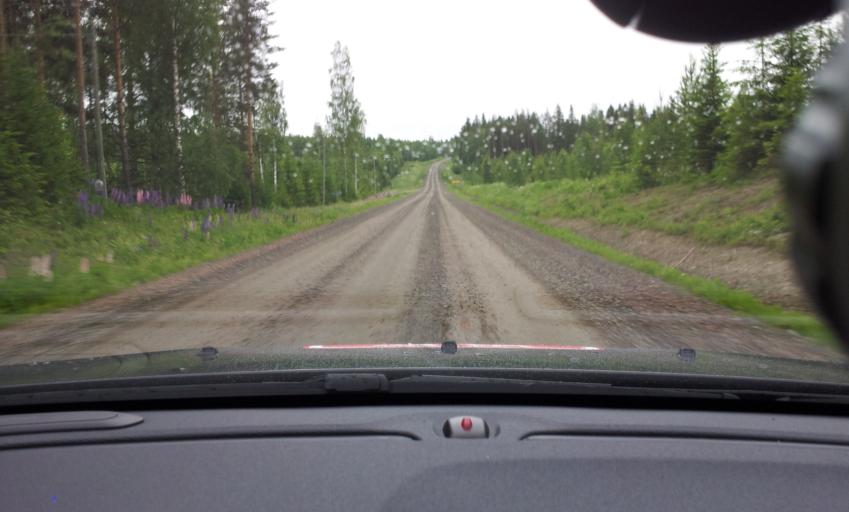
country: SE
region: Jaemtland
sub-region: Ragunda Kommun
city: Hammarstrand
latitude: 63.1293
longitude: 16.3234
